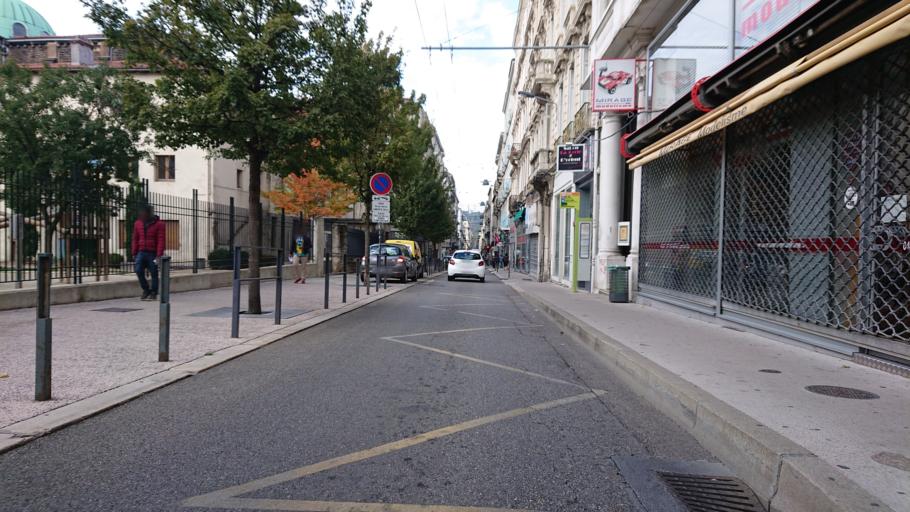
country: FR
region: Rhone-Alpes
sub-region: Departement de la Loire
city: Saint-Etienne
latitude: 45.4391
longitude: 4.3930
